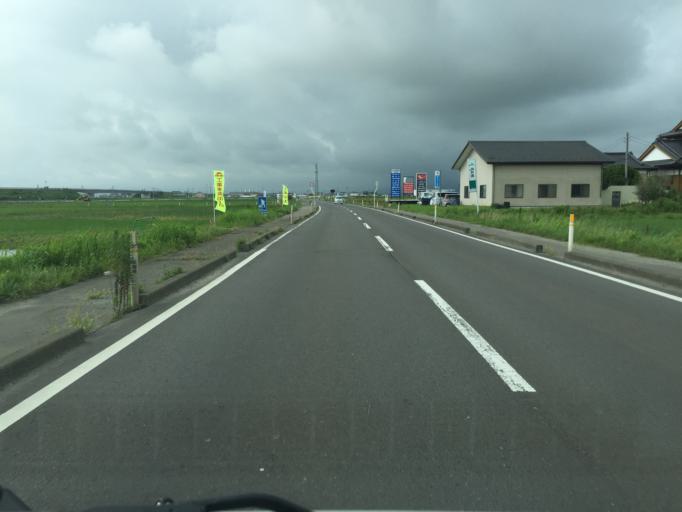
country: JP
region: Miyagi
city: Watari
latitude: 38.0398
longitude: 140.8898
